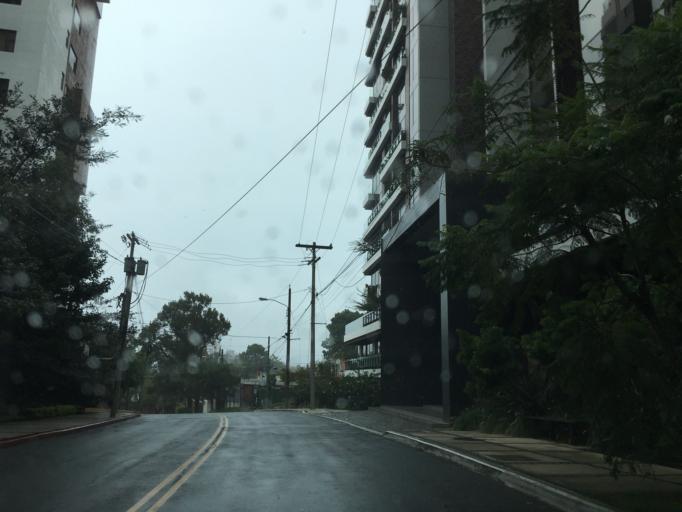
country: GT
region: Guatemala
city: Santa Catarina Pinula
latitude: 14.5845
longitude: -90.4889
